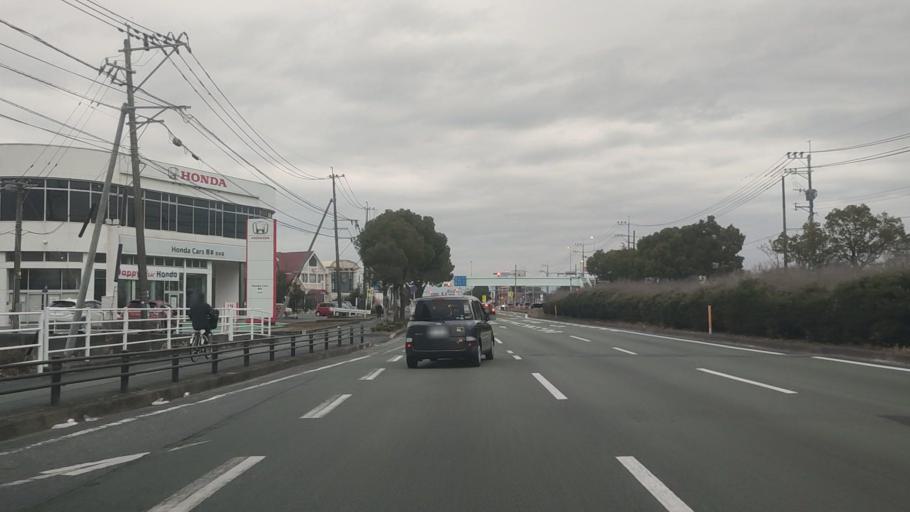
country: JP
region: Kumamoto
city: Kumamoto
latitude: 32.7698
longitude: 130.7285
